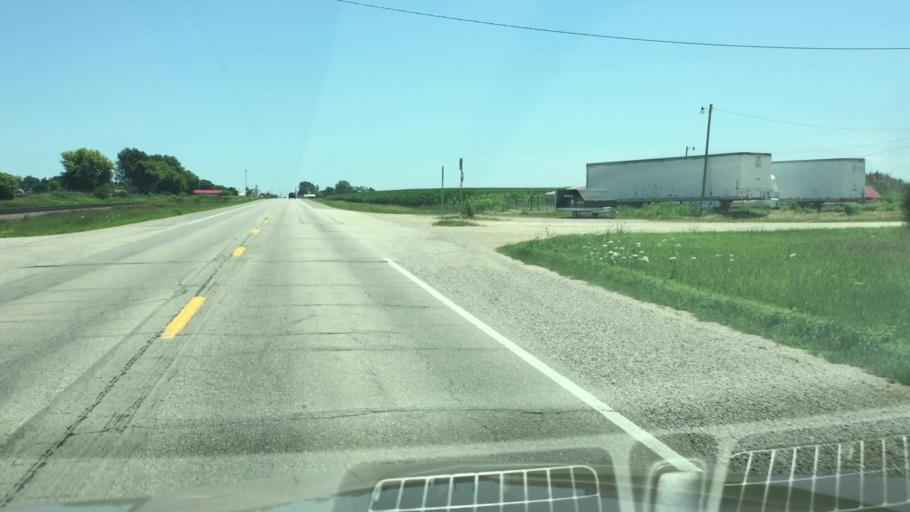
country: US
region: Iowa
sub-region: Cedar County
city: Mechanicsville
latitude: 41.9057
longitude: -91.2692
